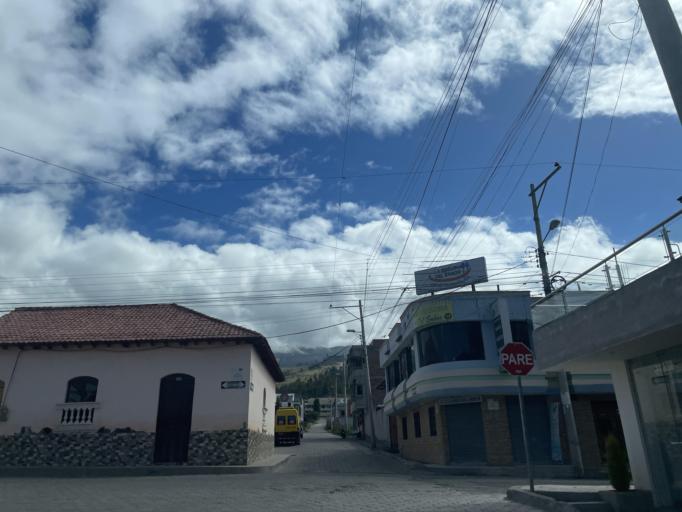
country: EC
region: Chimborazo
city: Guano
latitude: -1.6060
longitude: -78.6420
